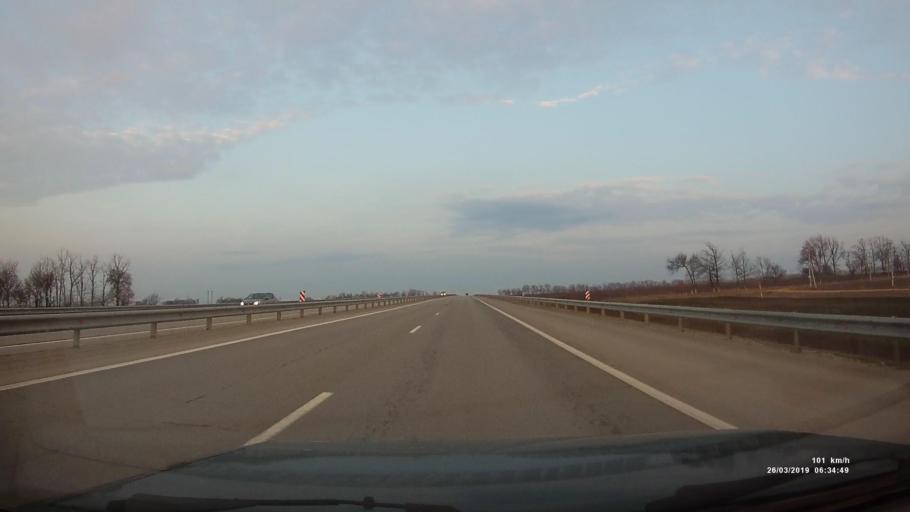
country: RU
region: Rostov
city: Chaltyr
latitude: 47.2783
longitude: 39.4579
